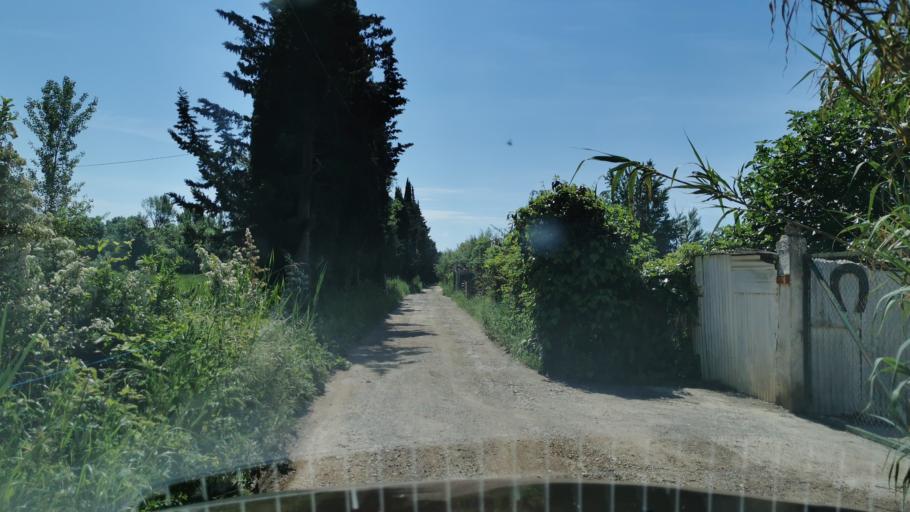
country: FR
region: Languedoc-Roussillon
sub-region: Departement de l'Aude
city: Narbonne
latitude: 43.1969
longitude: 3.0010
